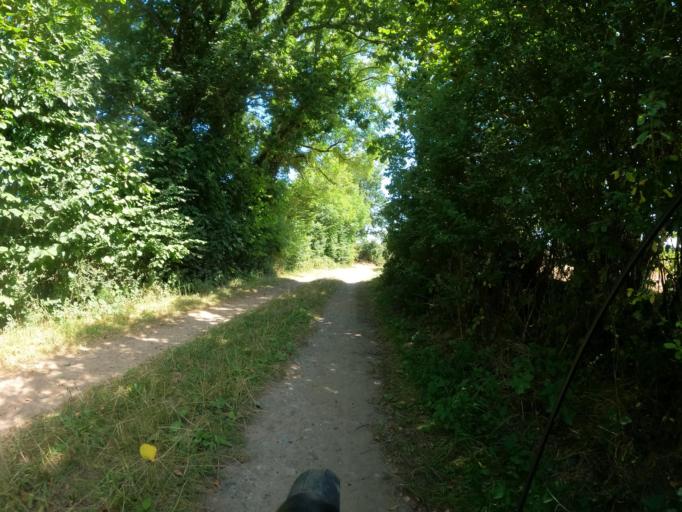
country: DE
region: Schleswig-Holstein
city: Quern
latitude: 54.7829
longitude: 9.7217
